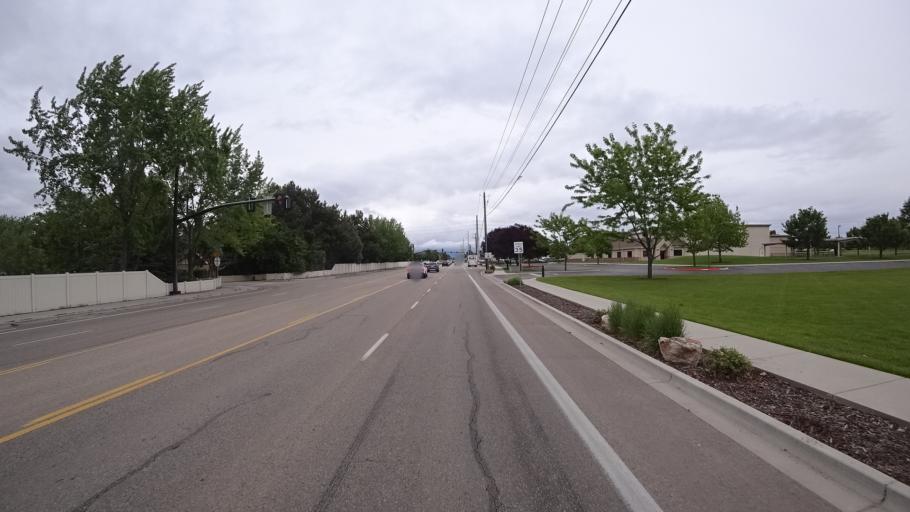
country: US
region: Idaho
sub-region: Ada County
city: Meridian
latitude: 43.6338
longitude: -116.3369
